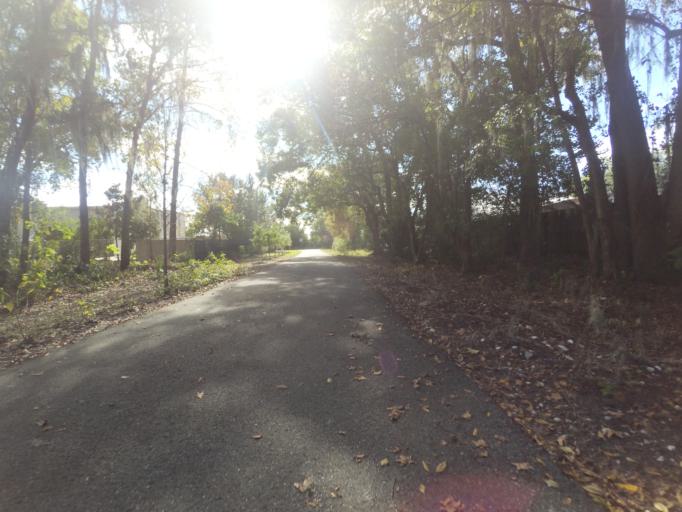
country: US
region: Florida
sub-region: Alachua County
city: Gainesville
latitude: 29.6656
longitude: -82.3262
